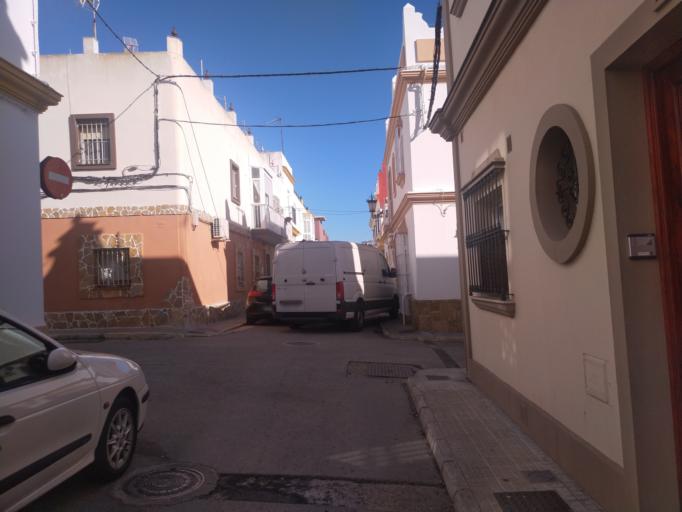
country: ES
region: Andalusia
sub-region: Provincia de Cadiz
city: San Fernando
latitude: 36.4720
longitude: -6.1971
